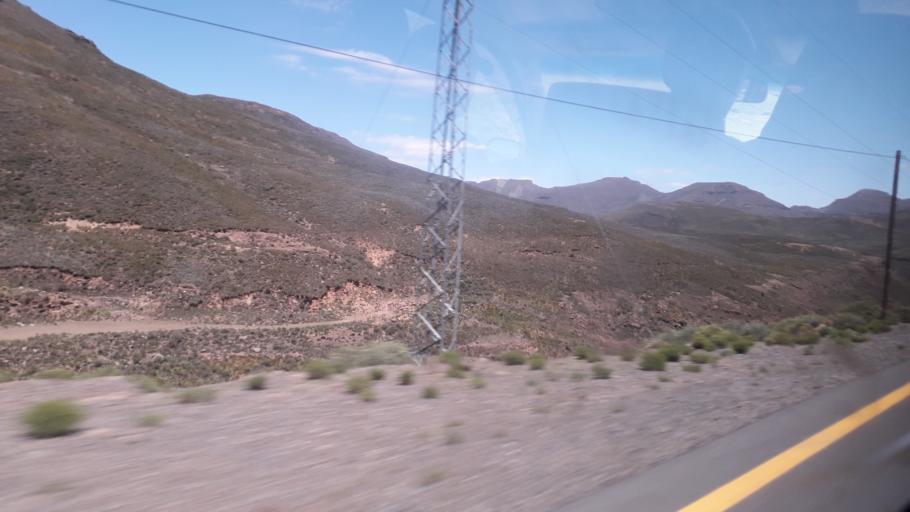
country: ZA
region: Orange Free State
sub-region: Thabo Mofutsanyana District Municipality
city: Phuthaditjhaba
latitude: -28.7674
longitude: 28.6611
